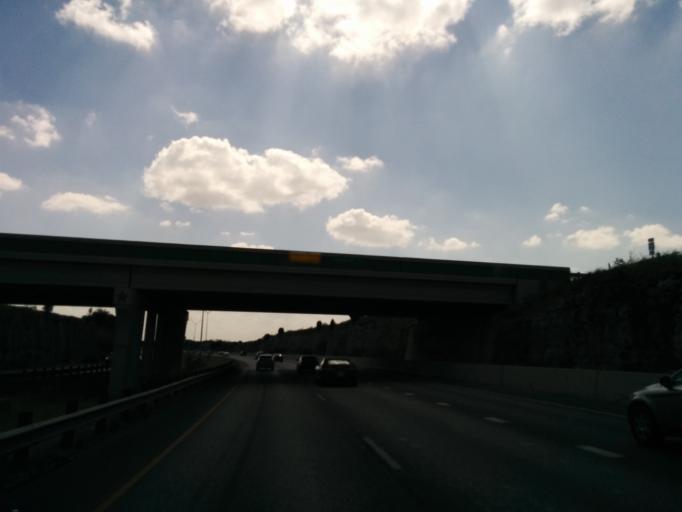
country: US
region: Texas
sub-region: Bexar County
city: Hollywood Park
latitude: 29.6086
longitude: -98.5224
